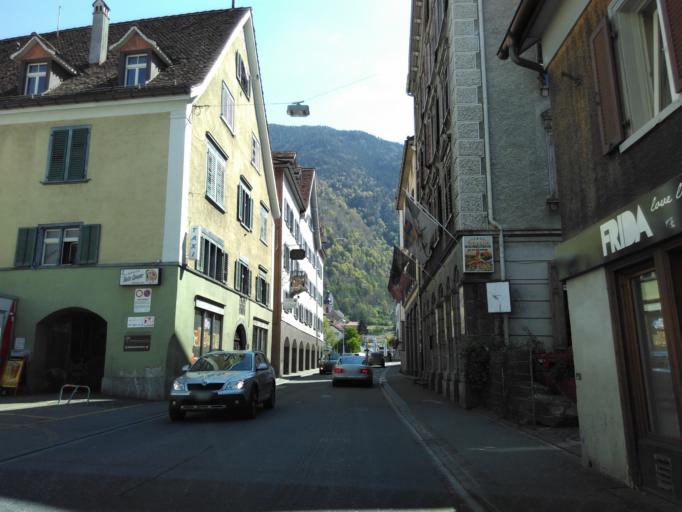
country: CH
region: Grisons
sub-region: Plessur District
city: Chur
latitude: 46.8477
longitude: 9.5282
